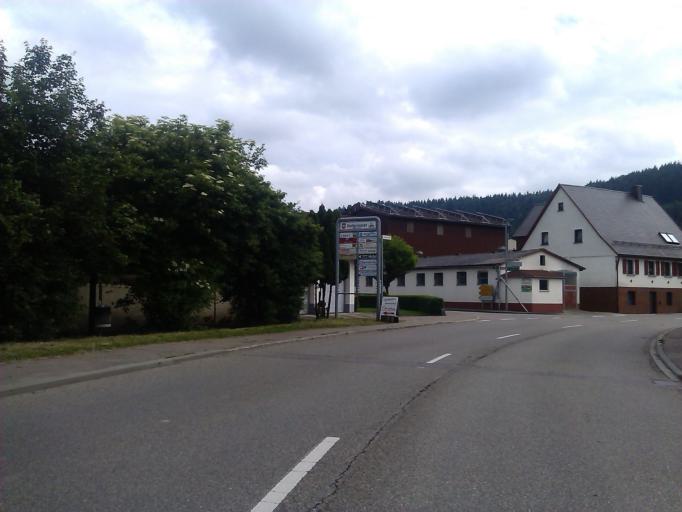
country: DE
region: Baden-Wuerttemberg
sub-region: Regierungsbezirk Stuttgart
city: Gaildorf
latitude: 48.9809
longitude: 9.7771
